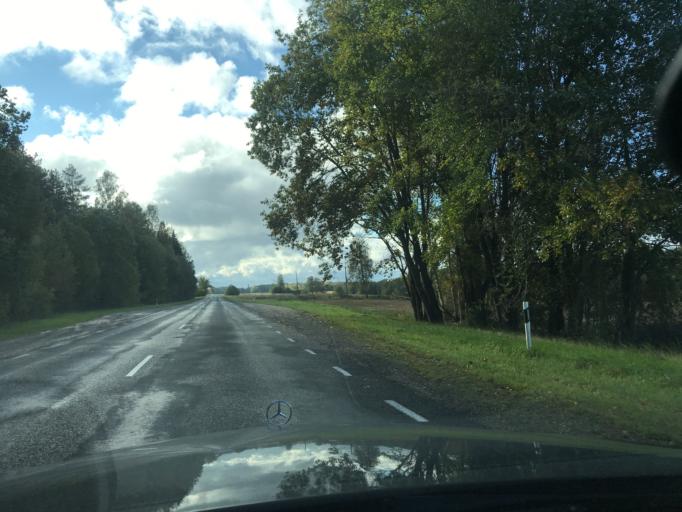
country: EE
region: Tartu
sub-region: Elva linn
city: Elva
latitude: 57.9826
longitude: 26.2616
